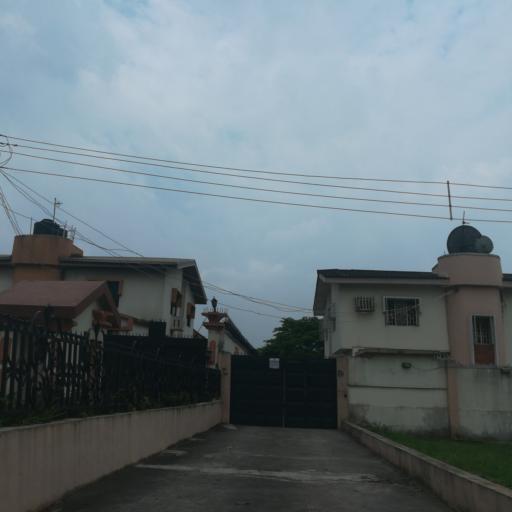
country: NG
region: Lagos
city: Ojota
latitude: 6.5809
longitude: 3.3836
